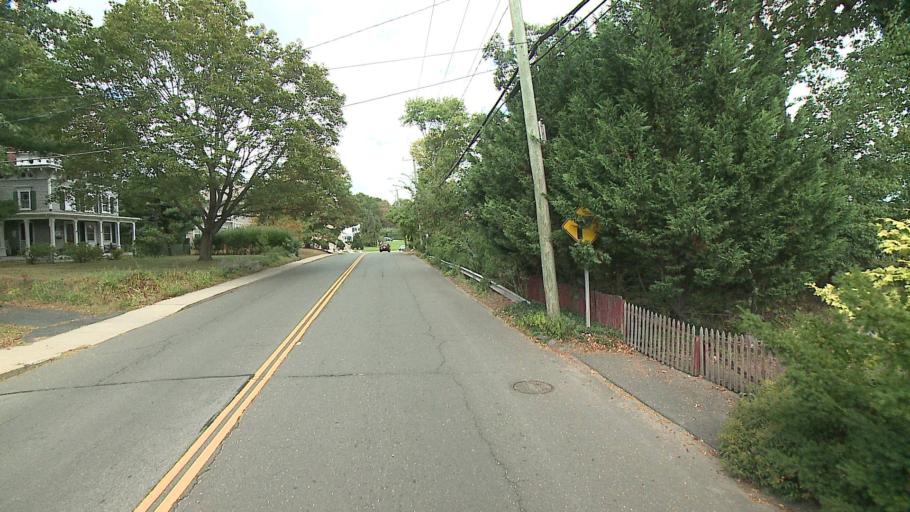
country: US
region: Connecticut
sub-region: Fairfield County
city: Westport
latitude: 41.1353
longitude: -73.3649
